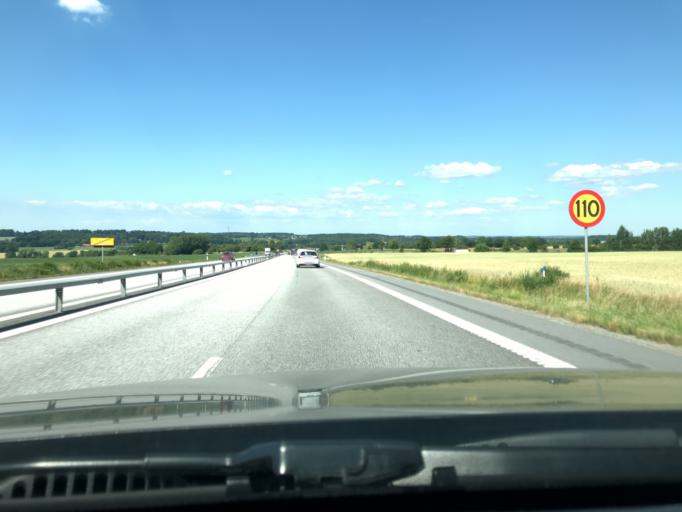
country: SE
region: Skane
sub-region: Hoors Kommun
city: Loberod
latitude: 55.7937
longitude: 13.4451
